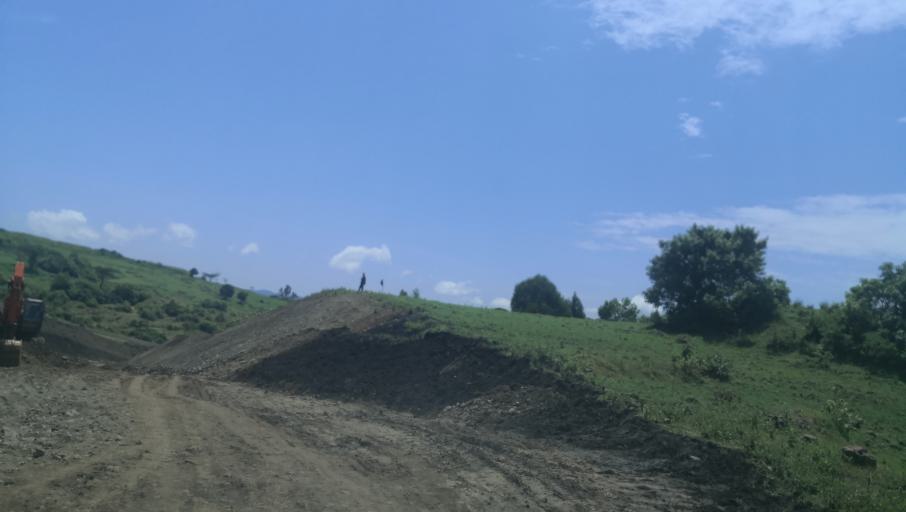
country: ET
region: Southern Nations, Nationalities, and People's Region
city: Butajira
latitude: 8.2729
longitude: 38.4881
